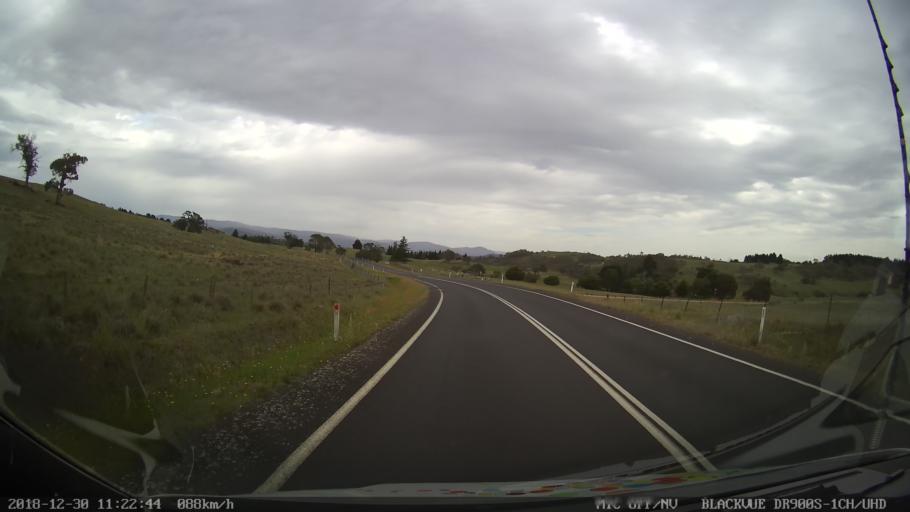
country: AU
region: New South Wales
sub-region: Snowy River
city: Jindabyne
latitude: -36.4959
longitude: 148.6705
